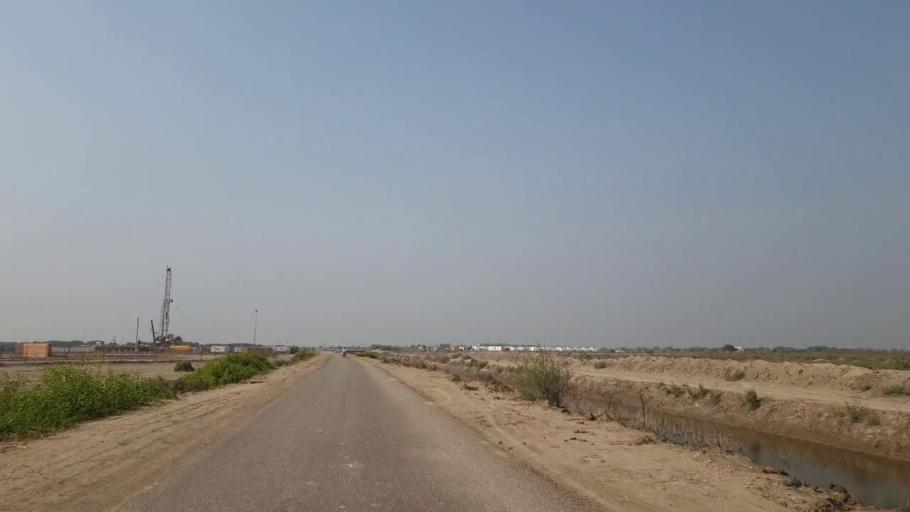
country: PK
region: Sindh
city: Tando Muhammad Khan
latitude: 24.9672
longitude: 68.5129
